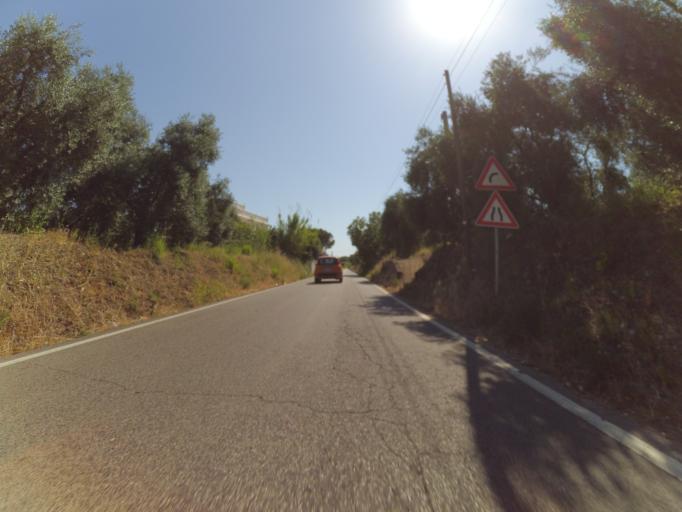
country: IT
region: Latium
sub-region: Provincia di Latina
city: Gaeta
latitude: 41.2300
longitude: 13.5106
